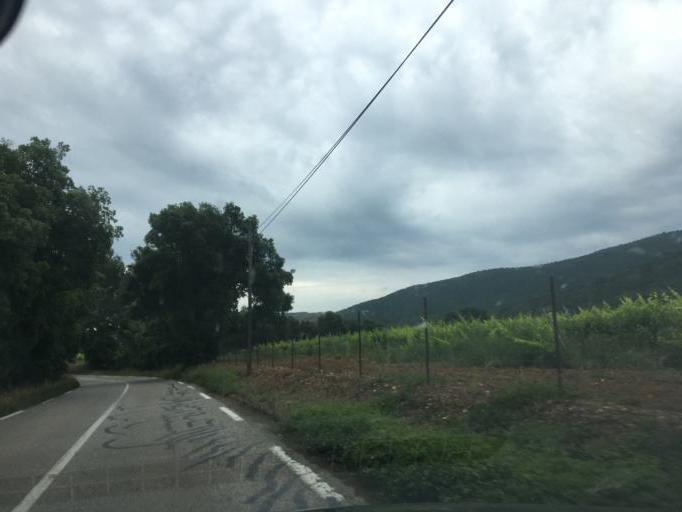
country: FR
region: Provence-Alpes-Cote d'Azur
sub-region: Departement du Var
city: Pierrefeu-du-Var
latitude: 43.2333
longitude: 6.1919
